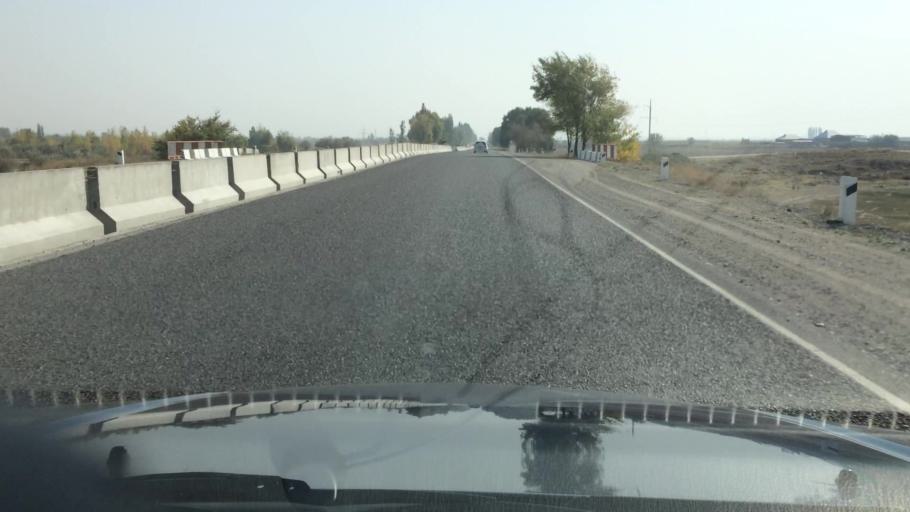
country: KG
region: Chuy
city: Kant
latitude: 42.9704
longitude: 74.9029
